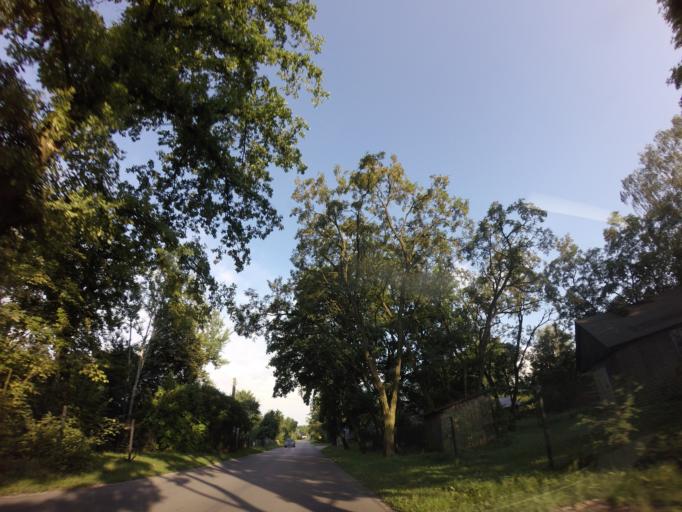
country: PL
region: Lublin Voivodeship
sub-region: Powiat pulawski
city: Kurow
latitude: 51.4235
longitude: 22.2259
